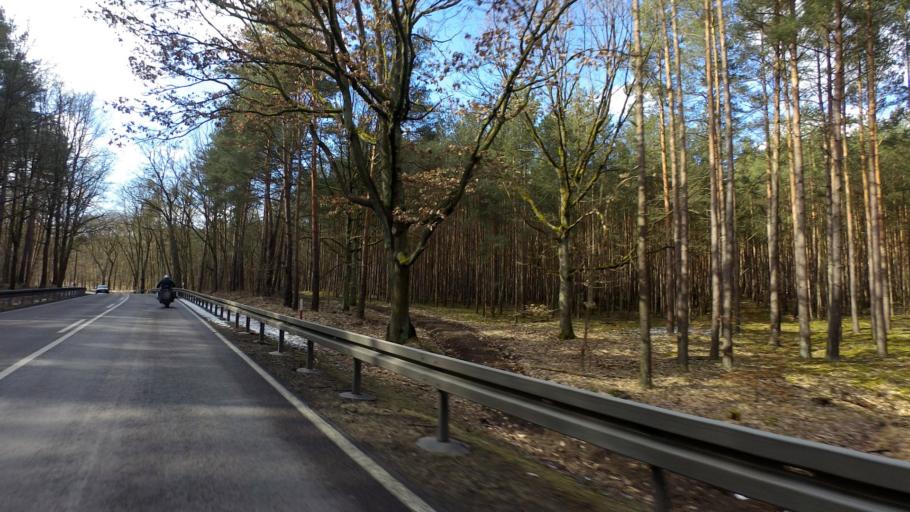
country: DE
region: Brandenburg
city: Marienwerder
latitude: 52.8580
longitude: 13.6246
